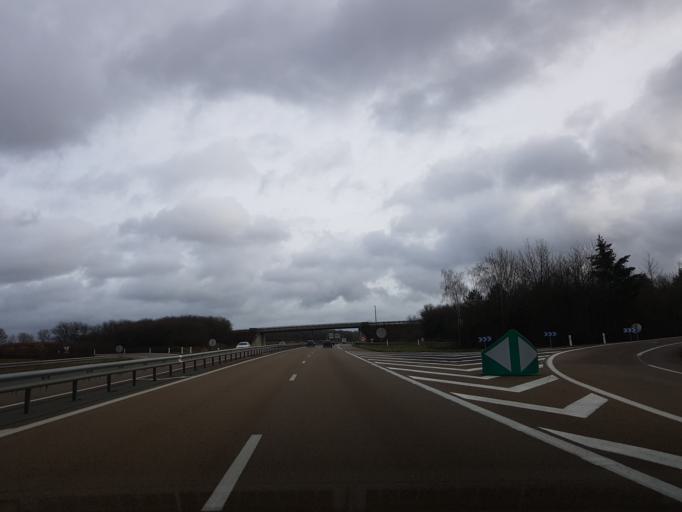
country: FR
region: Champagne-Ardenne
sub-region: Departement de la Haute-Marne
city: Chamarandes-Choignes
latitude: 48.0402
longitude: 5.0582
